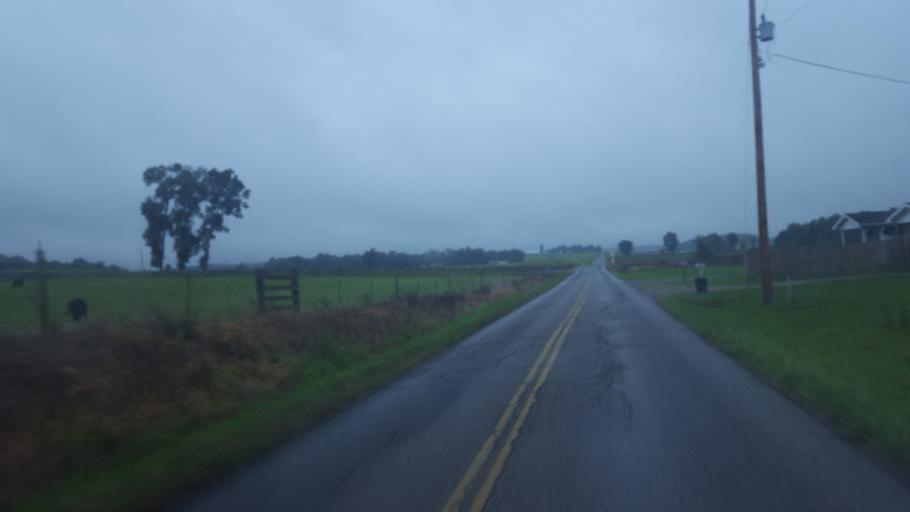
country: US
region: Ohio
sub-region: Jackson County
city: Oak Hill
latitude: 38.9499
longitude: -82.6019
